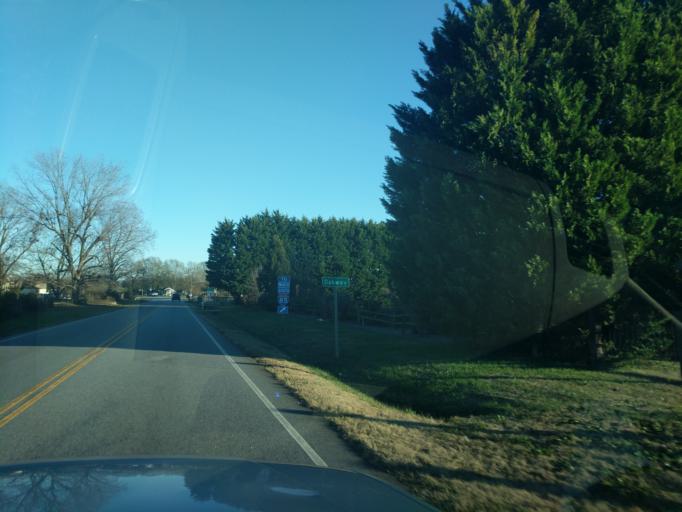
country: US
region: South Carolina
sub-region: Oconee County
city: Westminster
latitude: 34.6027
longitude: -83.0305
